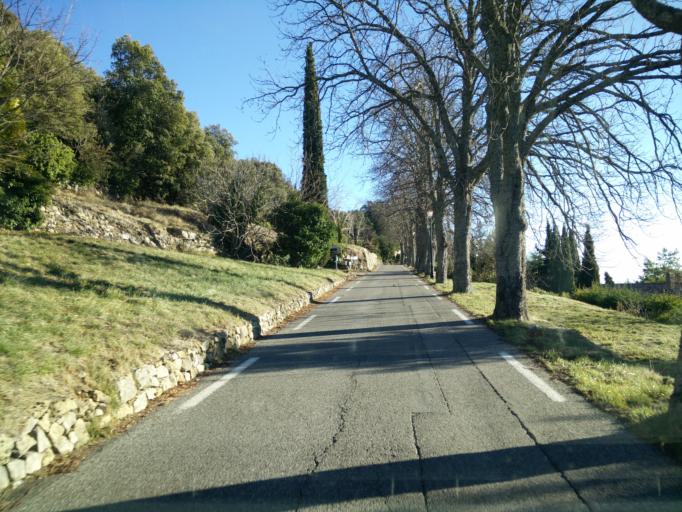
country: FR
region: Provence-Alpes-Cote d'Azur
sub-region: Departement du Var
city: Villecroze
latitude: 43.5917
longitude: 6.2995
